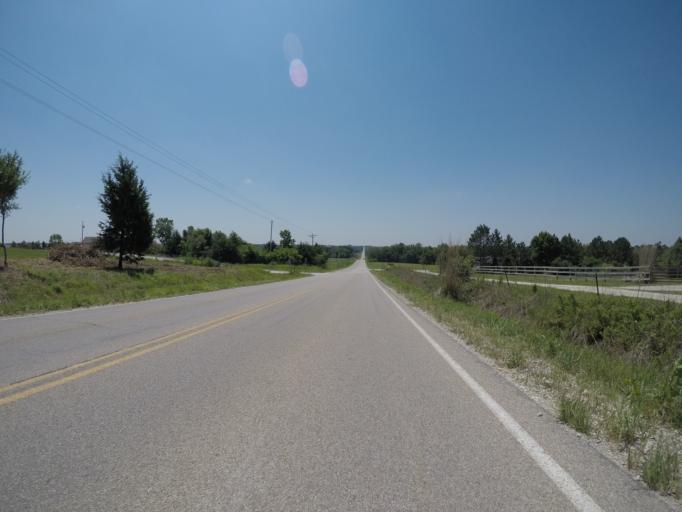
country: US
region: Kansas
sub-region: Pottawatomie County
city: Westmoreland
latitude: 39.2565
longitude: -96.4452
